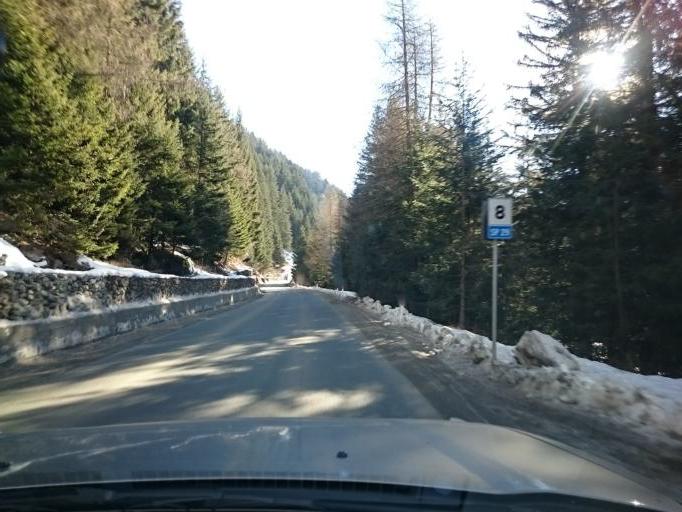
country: IT
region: Lombardy
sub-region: Provincia di Sondrio
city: Sant'Antonio
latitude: 46.4372
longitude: 10.4524
